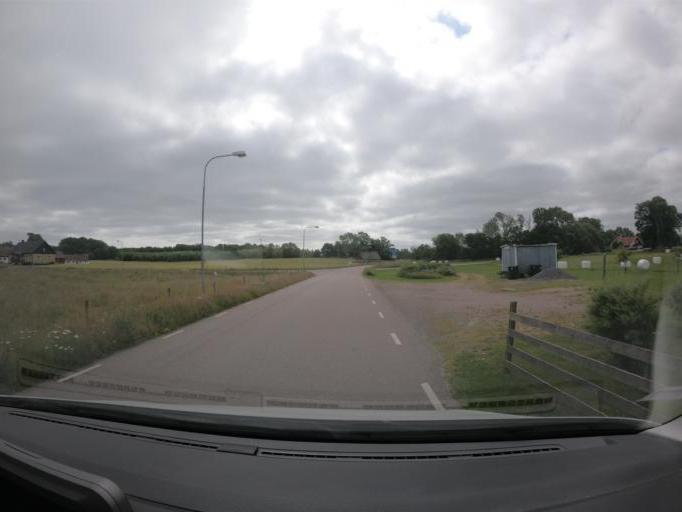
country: SE
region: Skane
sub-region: Hoors Kommun
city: Hoeoer
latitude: 55.9800
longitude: 13.4479
